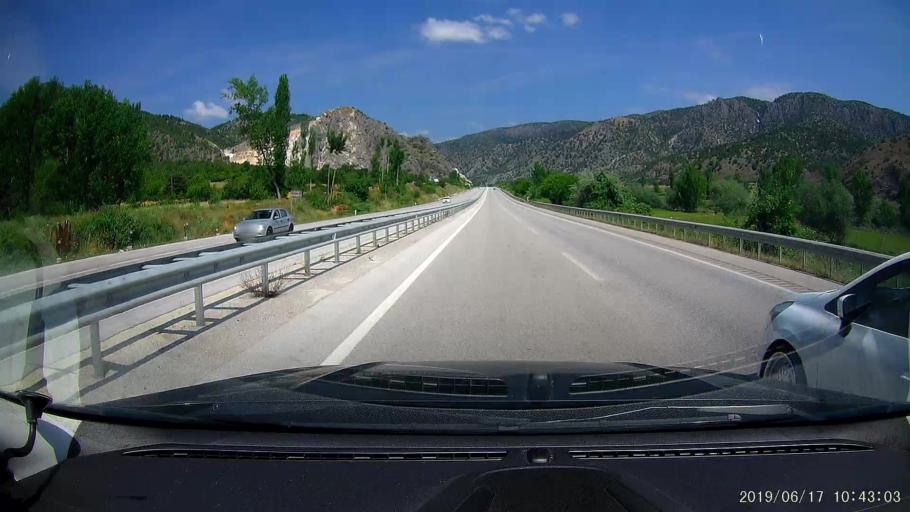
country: TR
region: Corum
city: Kargi
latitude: 41.0575
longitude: 34.5424
